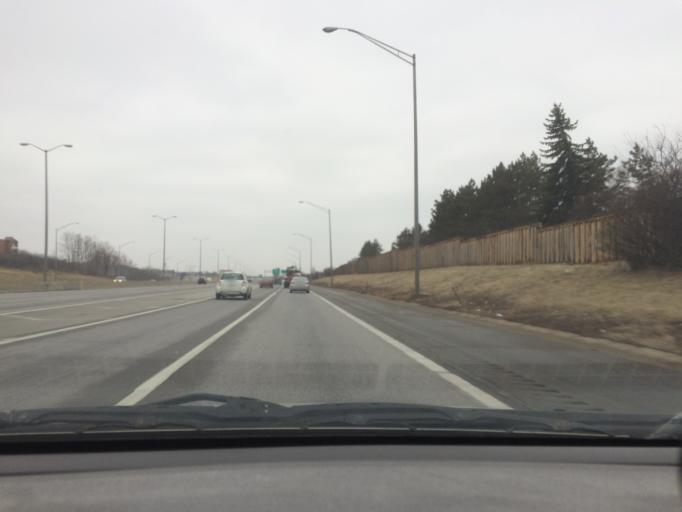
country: US
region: Illinois
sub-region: DuPage County
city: Downers Grove
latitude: 41.8414
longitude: -88.0295
